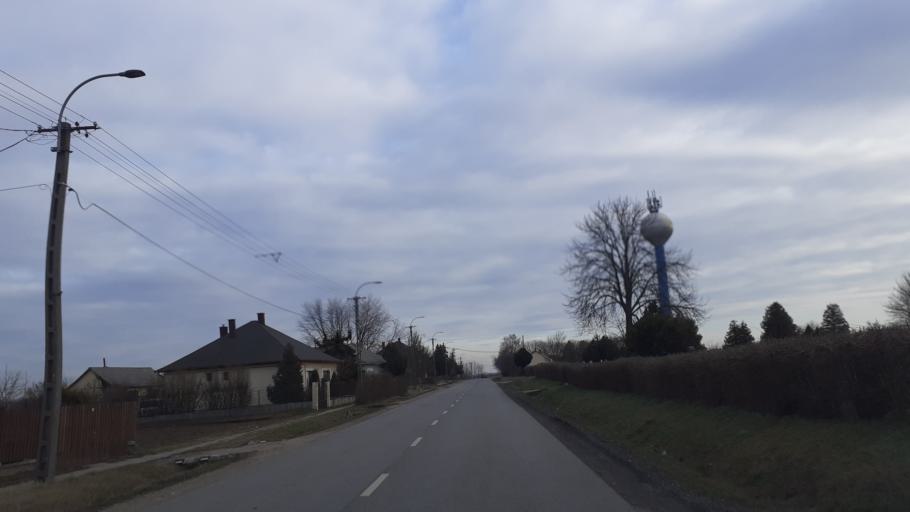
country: HU
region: Fejer
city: Sarkeresztur
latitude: 47.0017
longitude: 18.5523
